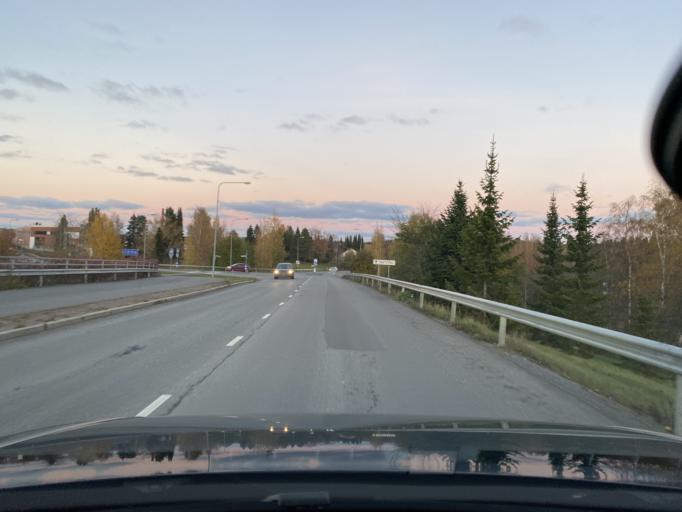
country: FI
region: Pirkanmaa
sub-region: Tampere
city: Lempaeaelae
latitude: 61.3274
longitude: 23.7594
